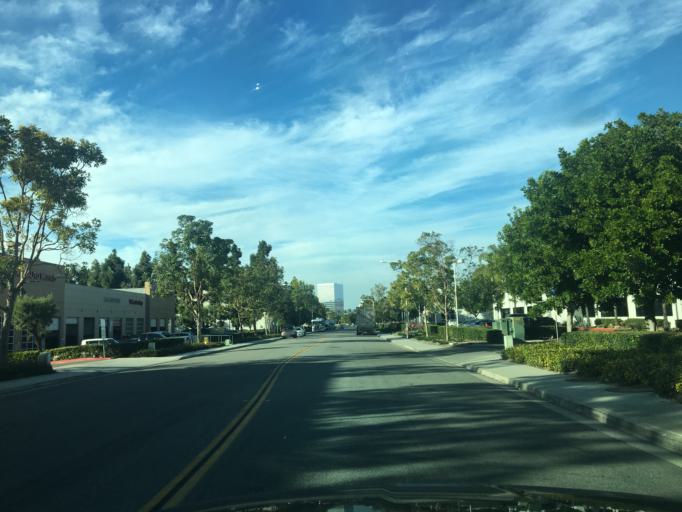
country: US
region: California
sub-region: Orange County
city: Laguna Woods
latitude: 33.6415
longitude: -117.7411
